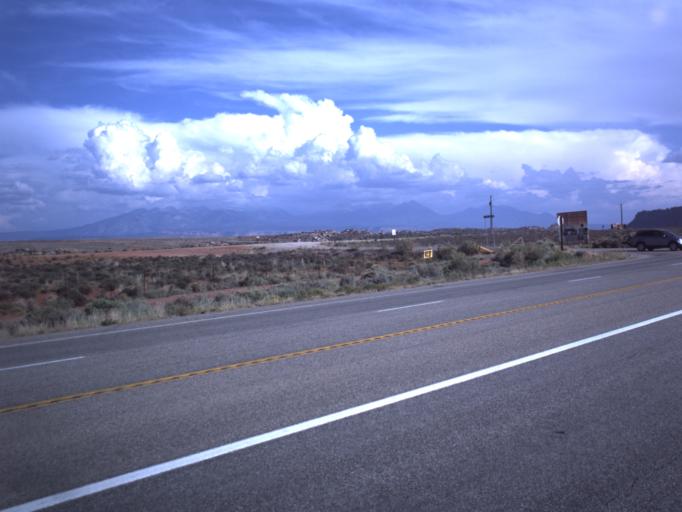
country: US
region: Utah
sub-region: Grand County
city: Moab
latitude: 38.6567
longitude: -109.6773
